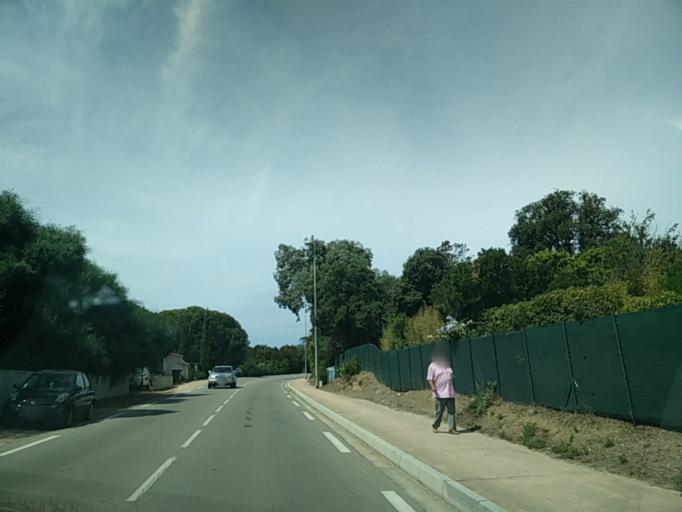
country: FR
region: Corsica
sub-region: Departement de la Corse-du-Sud
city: Pietrosella
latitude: 41.8350
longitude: 8.7773
